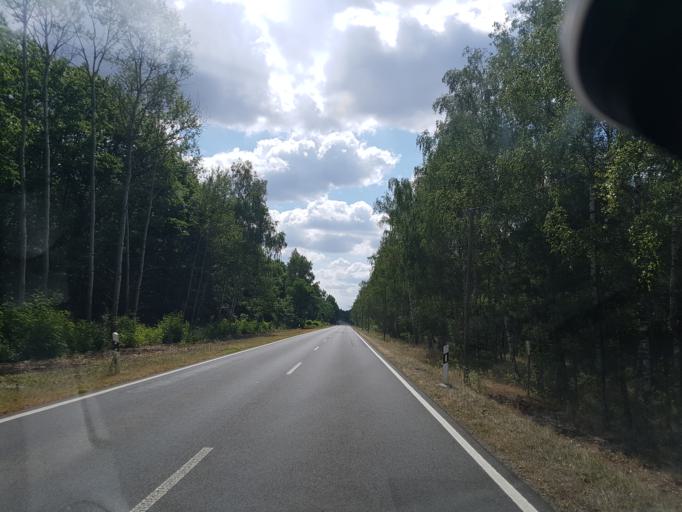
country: DE
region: Brandenburg
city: Drebkau
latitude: 51.6744
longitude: 14.1669
